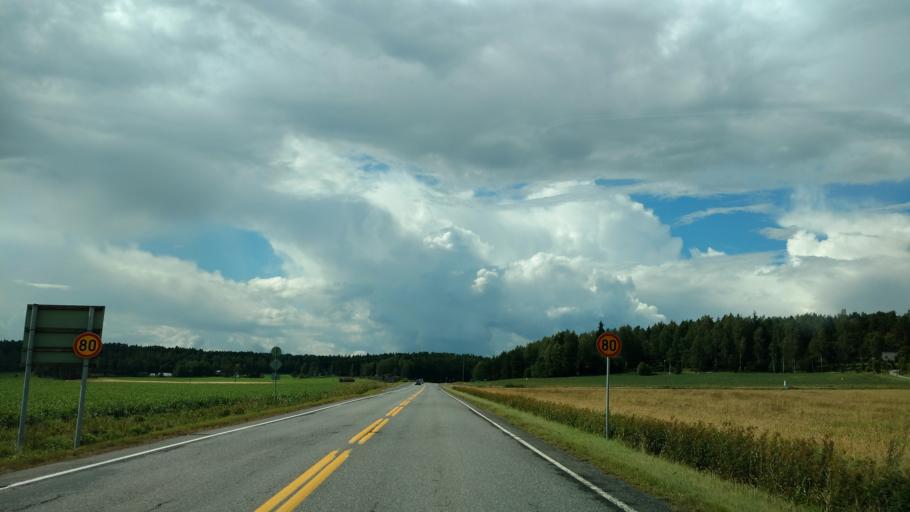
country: FI
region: Varsinais-Suomi
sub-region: Salo
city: Halikko
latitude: 60.3819
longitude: 22.8971
